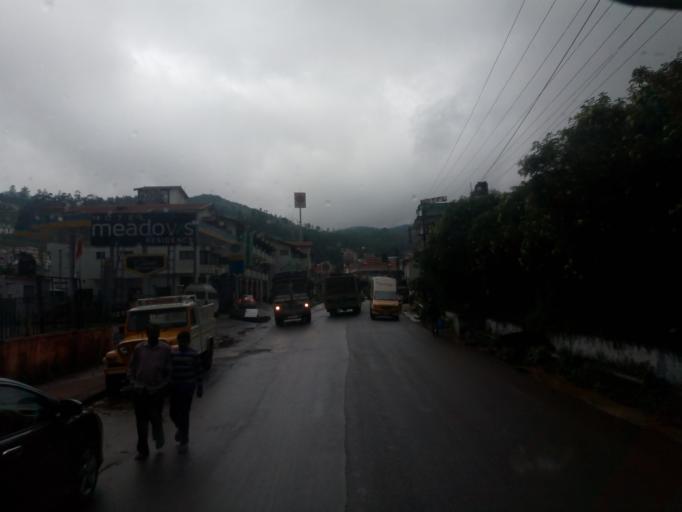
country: IN
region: Tamil Nadu
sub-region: Nilgiri
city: Ooty
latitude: 11.4111
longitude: 76.7104
